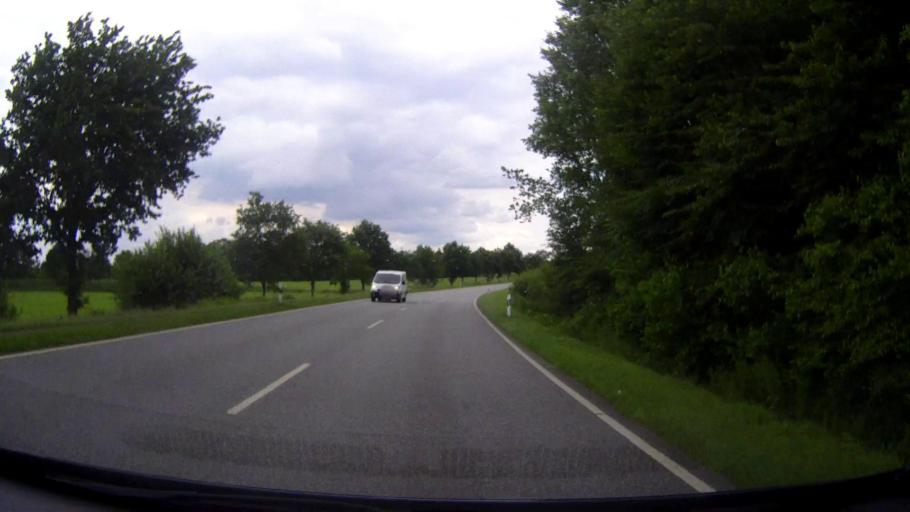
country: DE
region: Schleswig-Holstein
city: Reher
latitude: 54.0693
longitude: 9.5672
